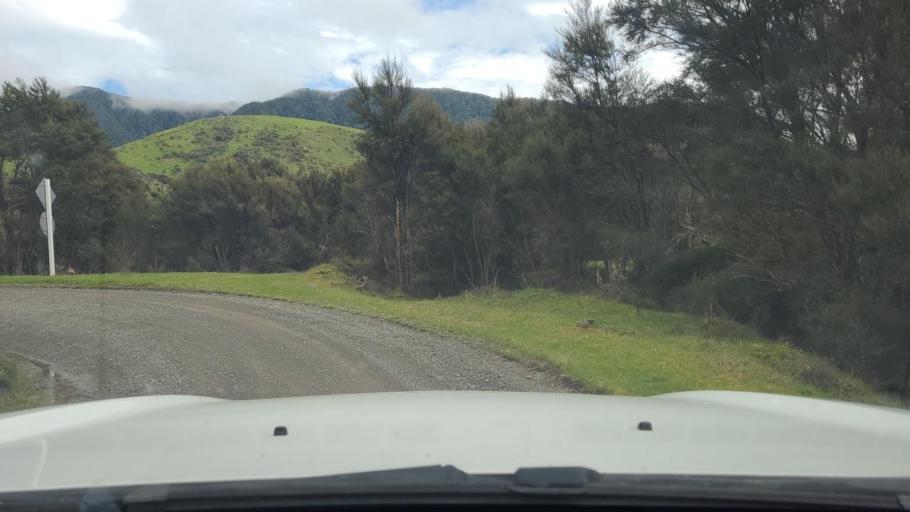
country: NZ
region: Wellington
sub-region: South Wairarapa District
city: Waipawa
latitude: -41.3842
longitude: 175.3744
